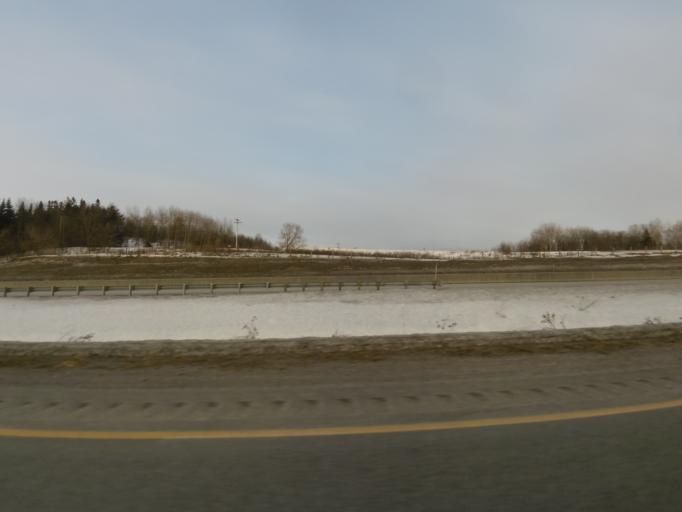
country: CA
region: Quebec
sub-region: Outaouais
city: Wakefield
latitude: 45.6309
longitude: -75.9393
